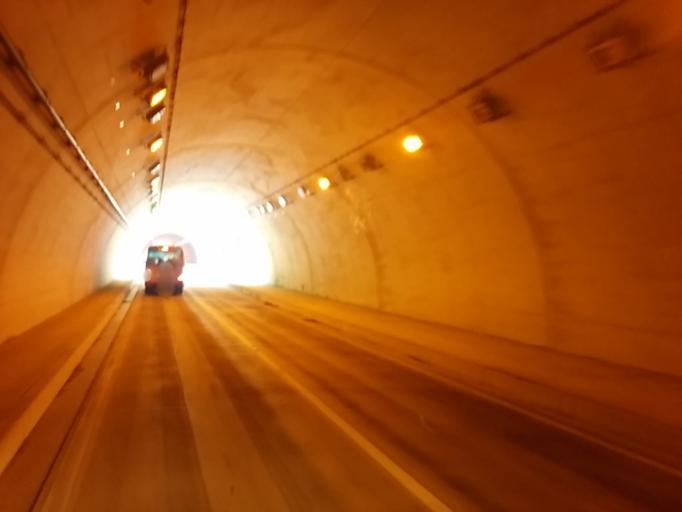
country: JP
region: Ehime
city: Niihama
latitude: 33.8869
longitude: 133.3055
